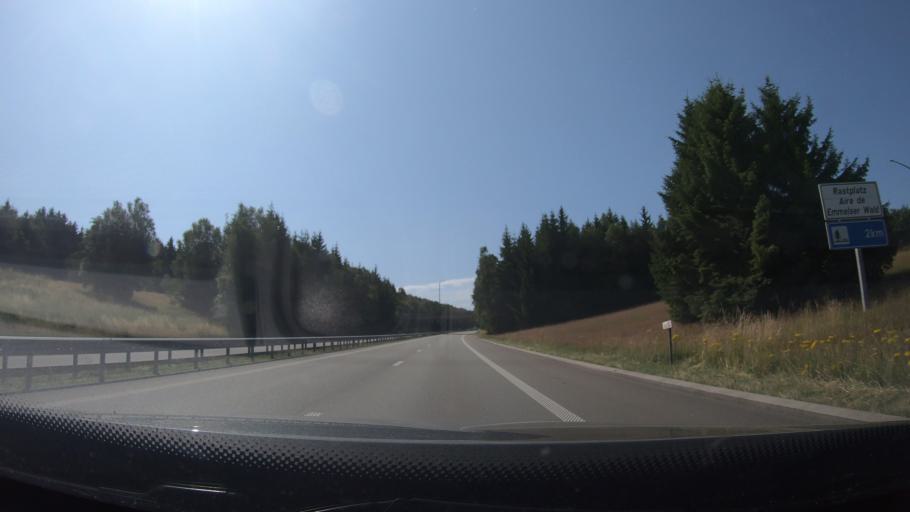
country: BE
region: Wallonia
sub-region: Province de Liege
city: Saint-Vith
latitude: 50.3397
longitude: 6.0880
